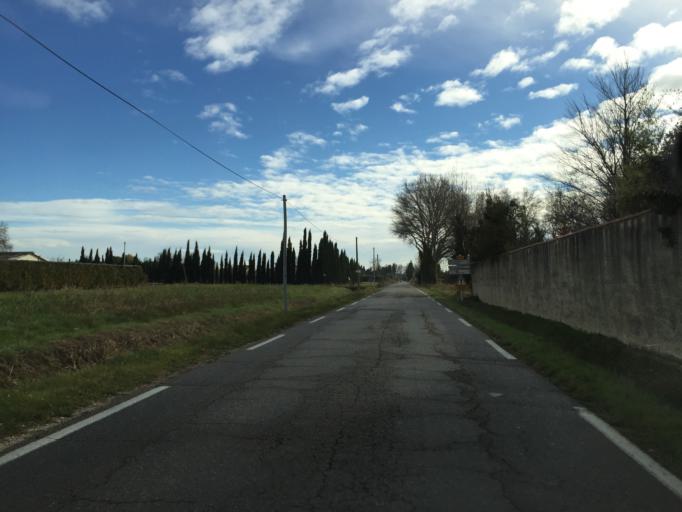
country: FR
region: Provence-Alpes-Cote d'Azur
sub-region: Departement du Vaucluse
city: Althen-des-Paluds
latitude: 43.9985
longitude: 4.9535
